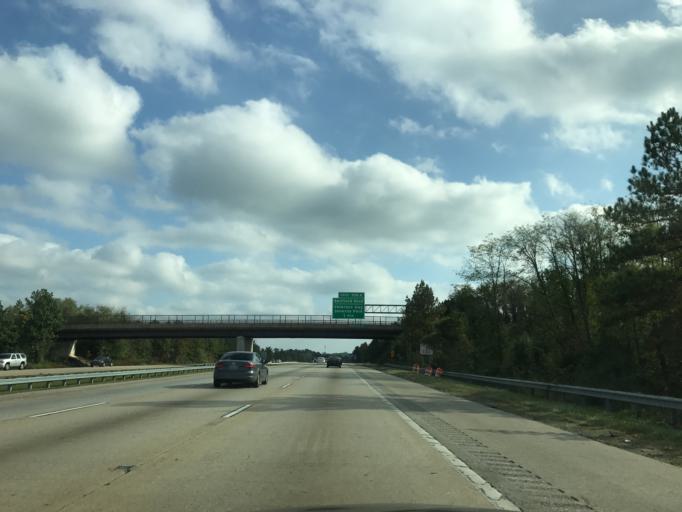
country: US
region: Maryland
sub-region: Anne Arundel County
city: South Gate
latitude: 39.1121
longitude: -76.6336
